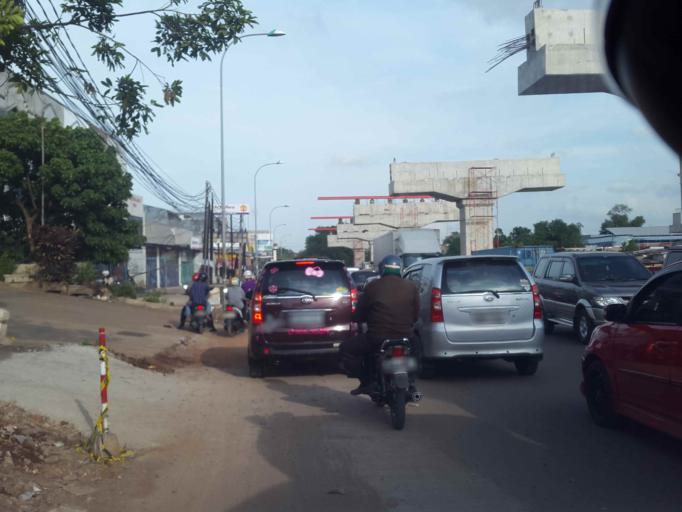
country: ID
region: West Java
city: Bekasi
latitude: -6.2497
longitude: 106.9466
